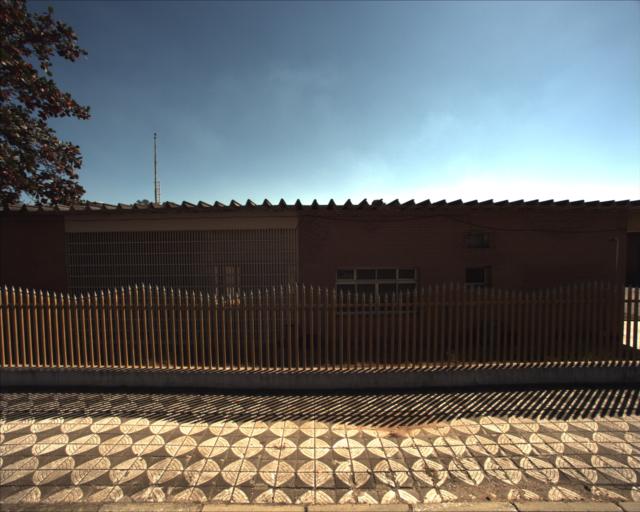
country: BR
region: Sao Paulo
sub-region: Sorocaba
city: Sorocaba
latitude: -23.4745
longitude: -47.4244
